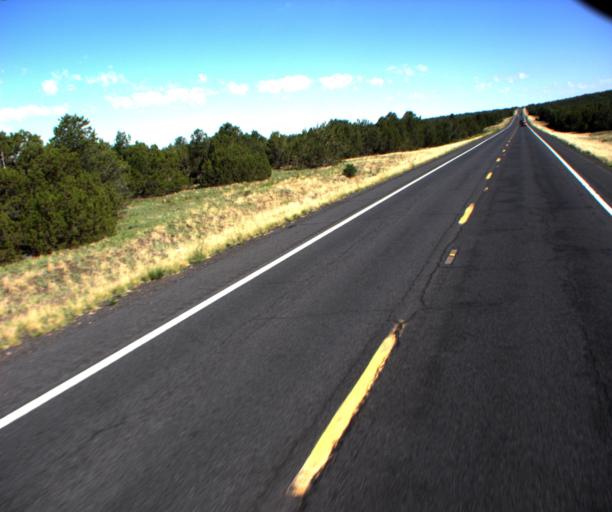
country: US
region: Arizona
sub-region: Coconino County
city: Williams
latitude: 35.3844
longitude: -112.1635
